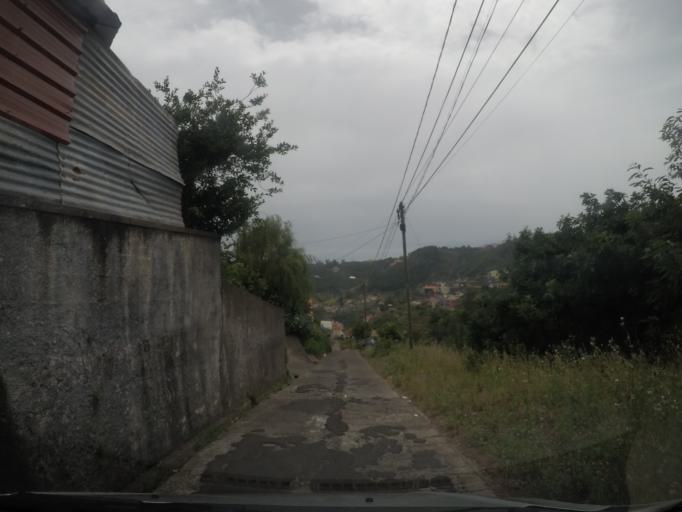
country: PT
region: Madeira
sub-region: Santa Cruz
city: Camacha
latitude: 32.6767
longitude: -16.8395
